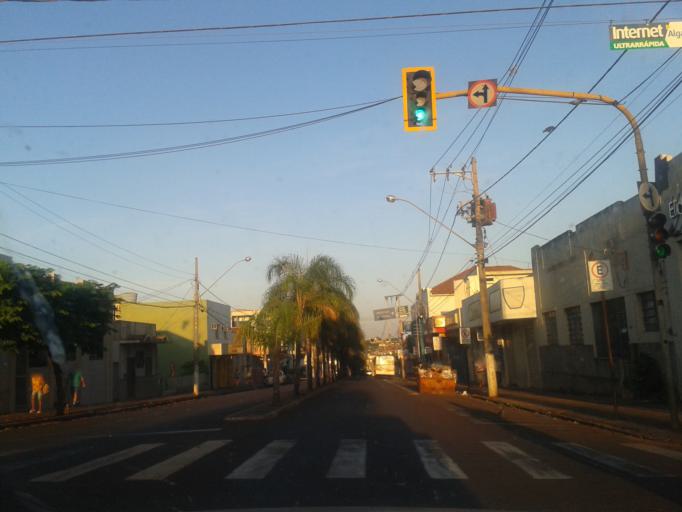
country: BR
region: Minas Gerais
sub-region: Ituiutaba
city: Ituiutaba
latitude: -18.9748
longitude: -49.4612
